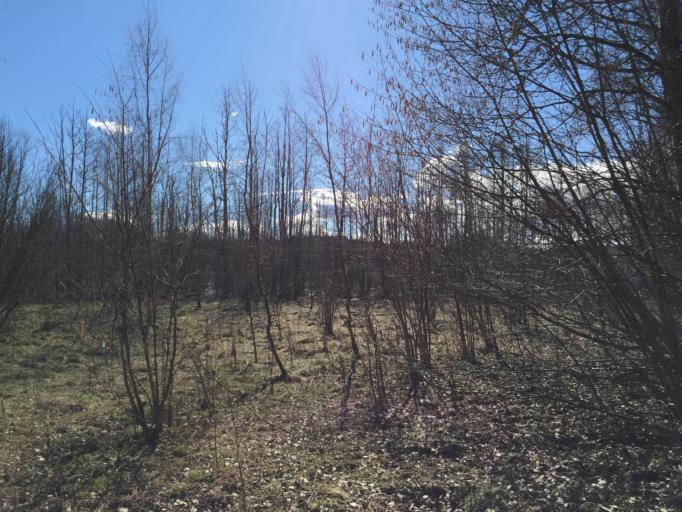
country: SE
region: OEstergoetland
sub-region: Finspangs Kommun
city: Finspang
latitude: 58.8827
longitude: 15.7615
